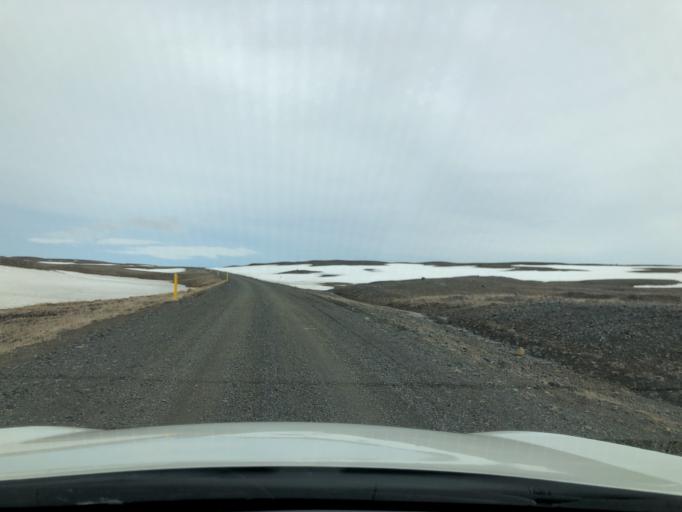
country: IS
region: East
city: Egilsstadir
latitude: 65.3034
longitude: -15.4003
